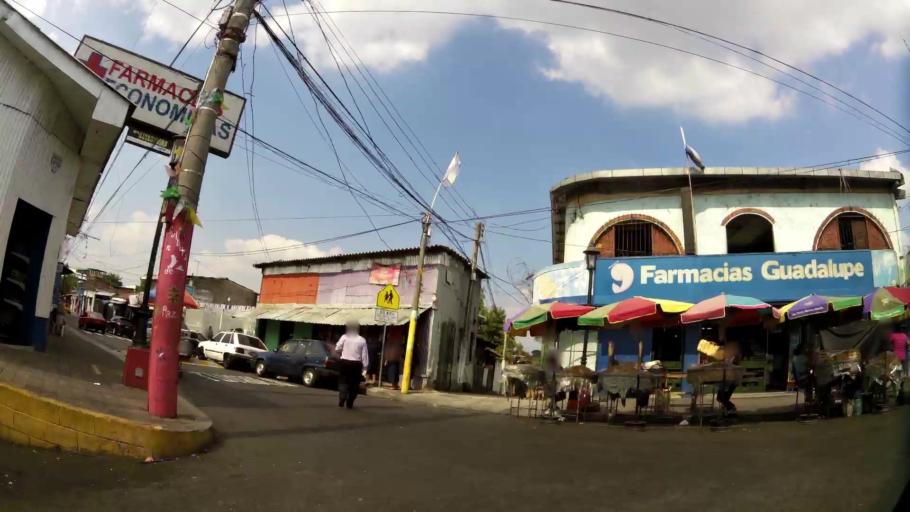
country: SV
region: San Salvador
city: Delgado
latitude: 13.7215
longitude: -89.1694
